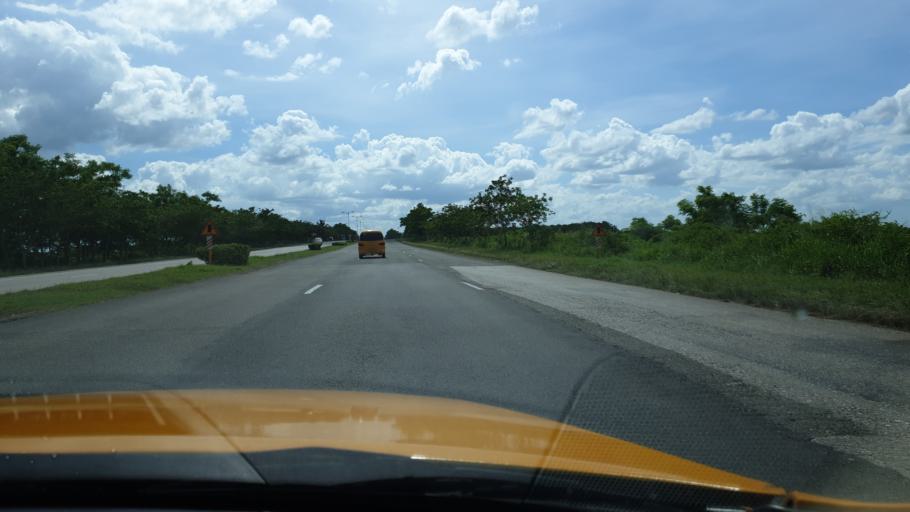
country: CU
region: Cienfuegos
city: Cruces
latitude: 22.4526
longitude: -80.2881
